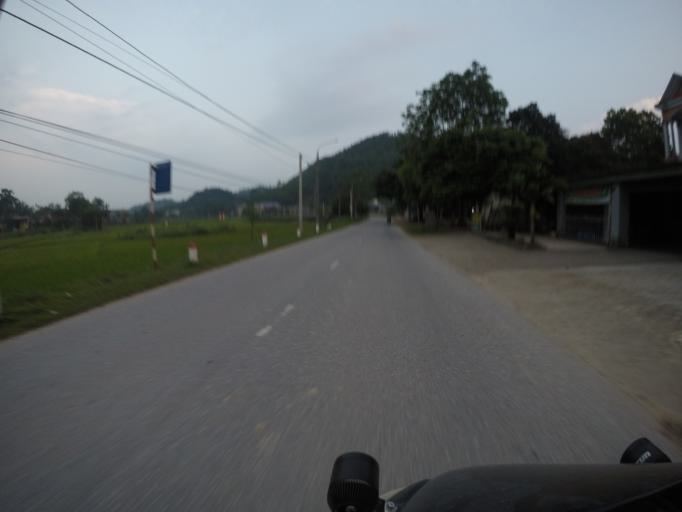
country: VN
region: Thai Nguyen
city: Chua Hang
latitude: 21.5901
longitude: 105.7300
